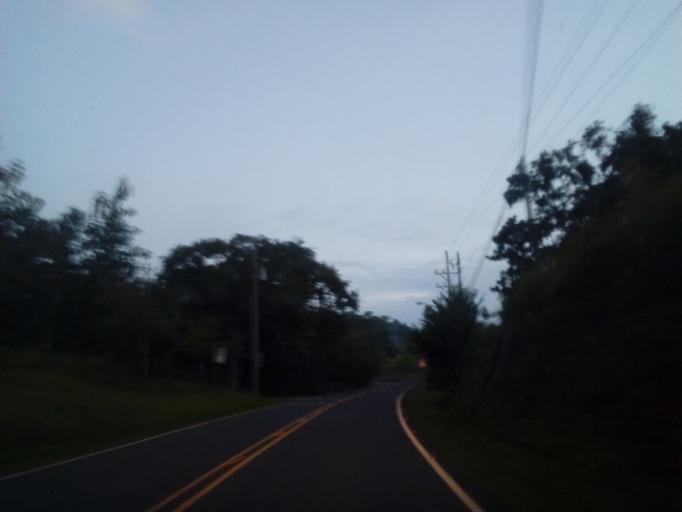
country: CR
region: Guanacaste
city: Samara
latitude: 9.9756
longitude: -85.5085
